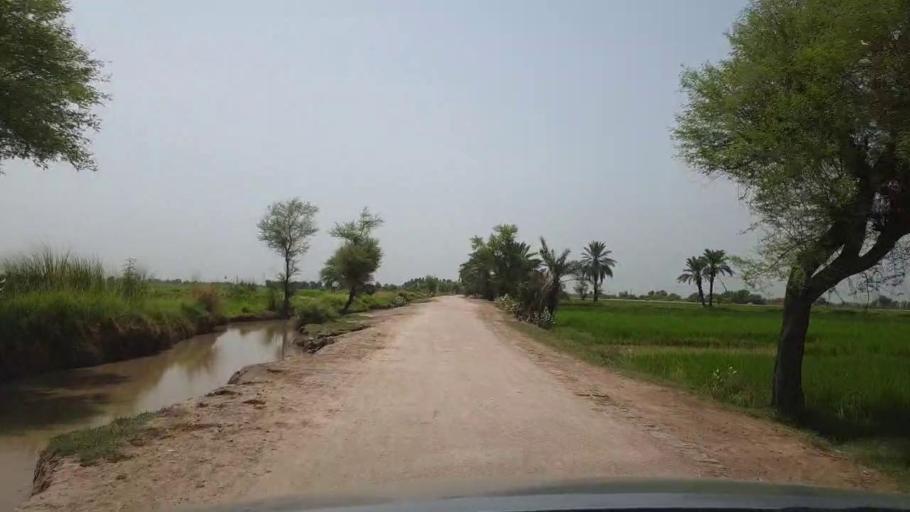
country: PK
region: Sindh
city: Madeji
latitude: 27.7787
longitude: 68.4324
